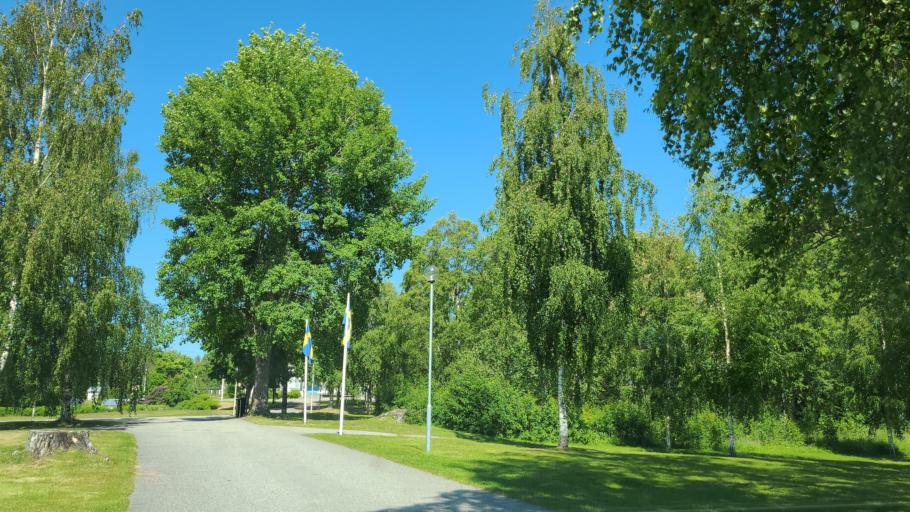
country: SE
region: Vaesternorrland
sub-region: OErnskoeldsviks Kommun
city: Husum
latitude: 63.3745
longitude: 19.1952
